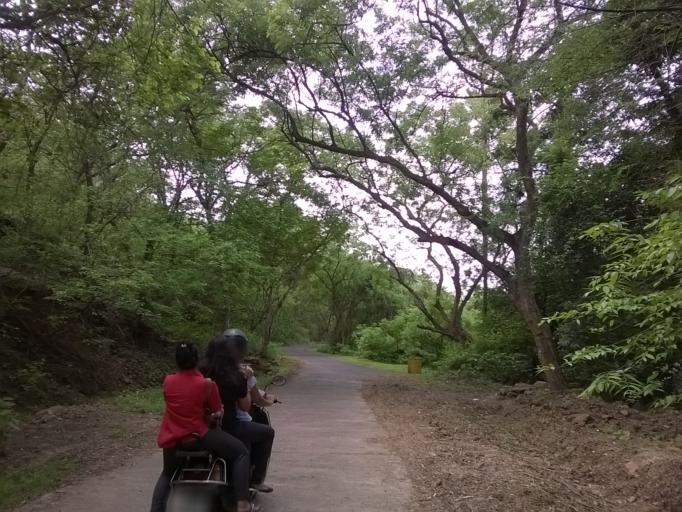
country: IN
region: Maharashtra
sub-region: Mumbai Suburban
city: Borivli
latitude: 19.2263
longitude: 72.8695
